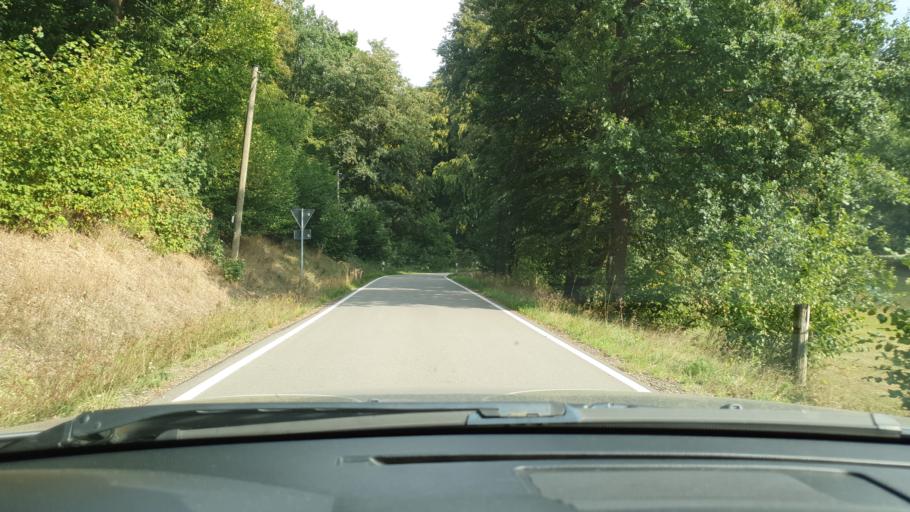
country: DE
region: Rheinland-Pfalz
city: Hettenhausen
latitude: 49.3463
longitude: 7.5368
